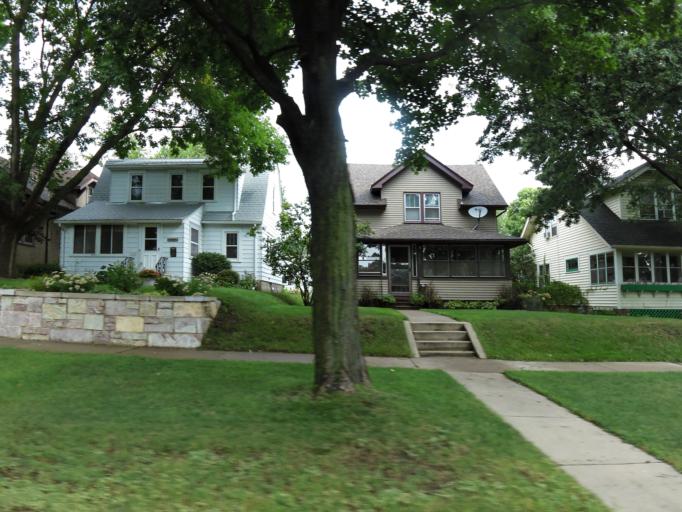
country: US
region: Minnesota
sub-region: Dakota County
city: Mendota Heights
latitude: 44.9307
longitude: -93.1605
